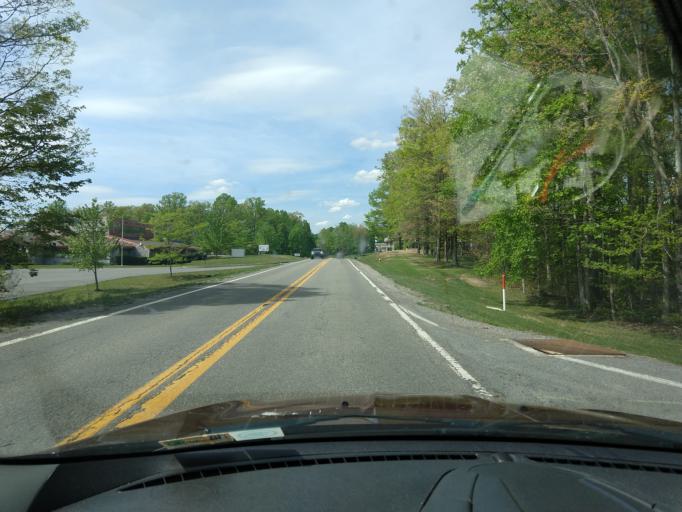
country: US
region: West Virginia
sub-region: Raleigh County
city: Daniels
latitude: 37.7873
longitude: -81.1164
